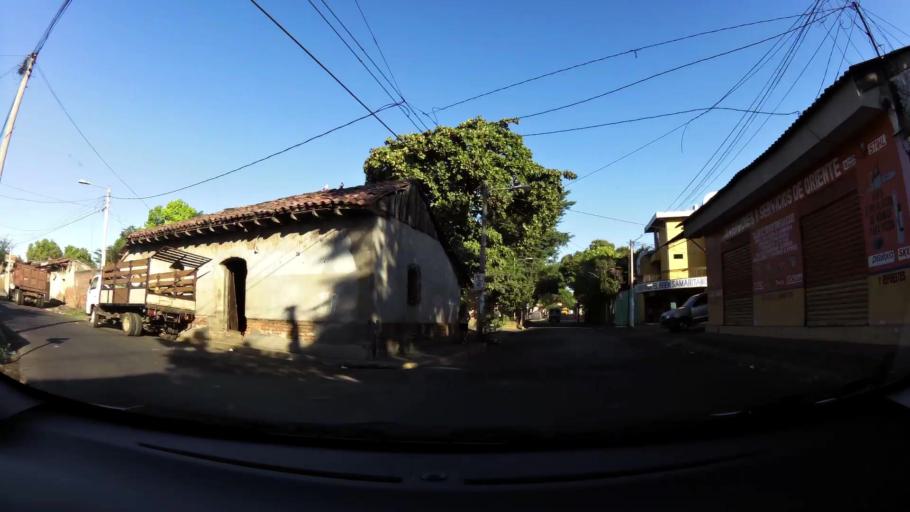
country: SV
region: San Miguel
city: San Miguel
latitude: 13.4855
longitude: -88.1709
